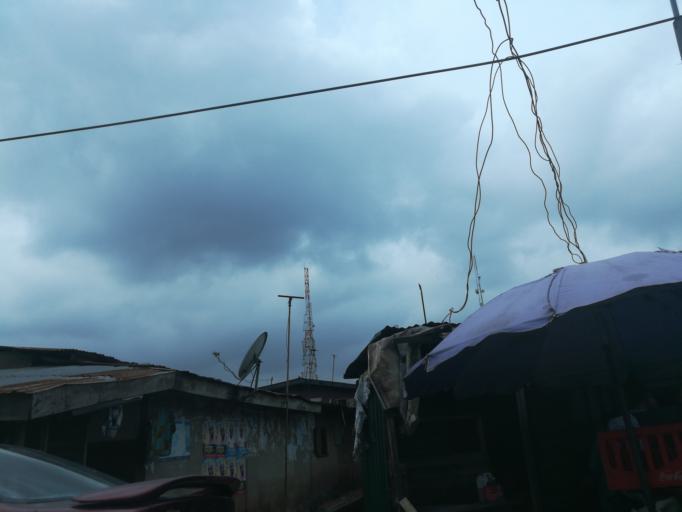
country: NG
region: Lagos
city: Ojota
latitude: 6.5702
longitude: 3.3640
